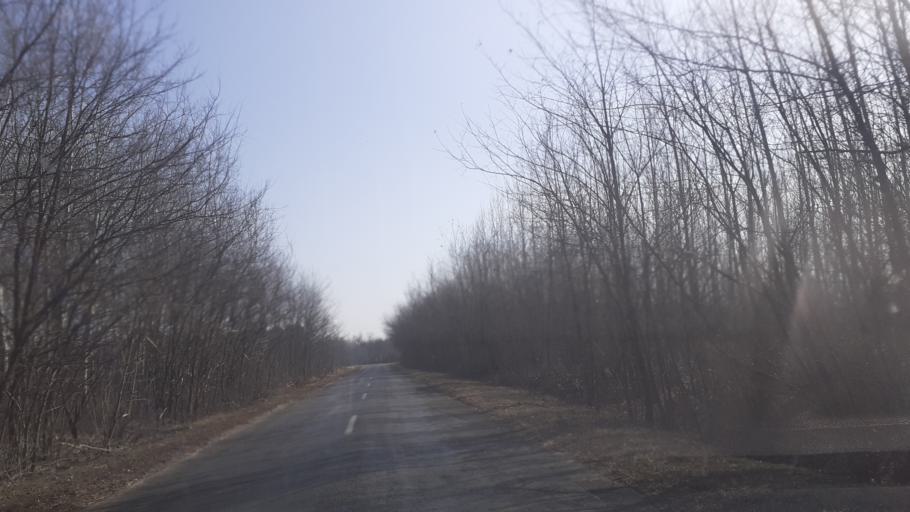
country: HU
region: Pest
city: Orkeny
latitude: 47.0556
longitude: 19.4120
